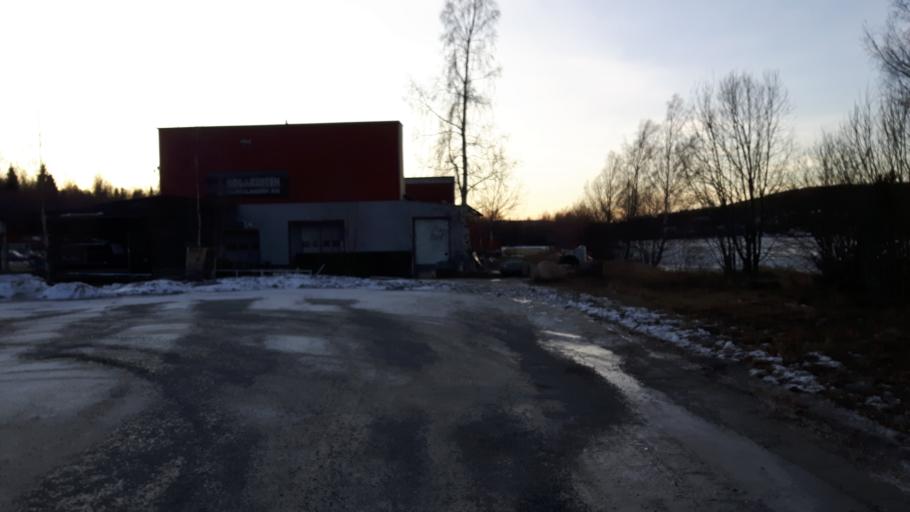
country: SE
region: Vaesternorrland
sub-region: Haernoesands Kommun
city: Haernoesand
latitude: 62.6226
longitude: 17.9435
